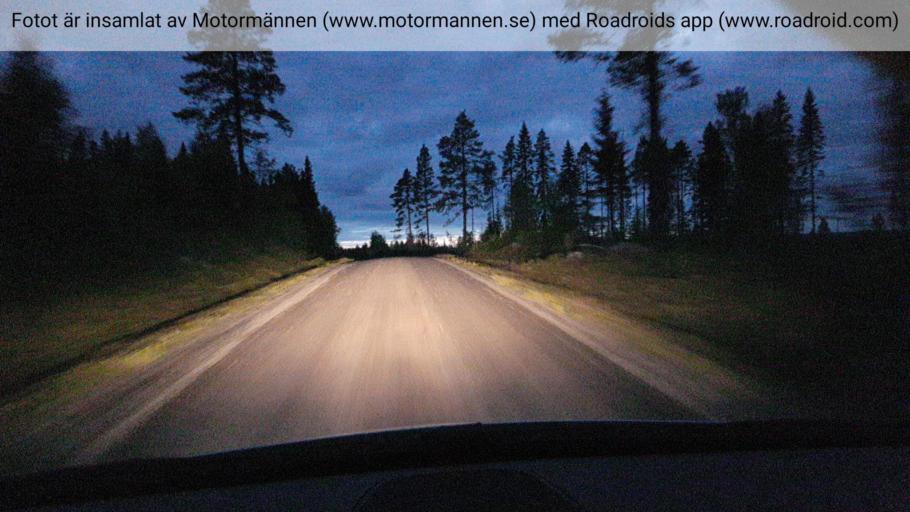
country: SE
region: Jaemtland
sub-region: OEstersunds Kommun
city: Lit
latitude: 63.2963
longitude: 15.3318
